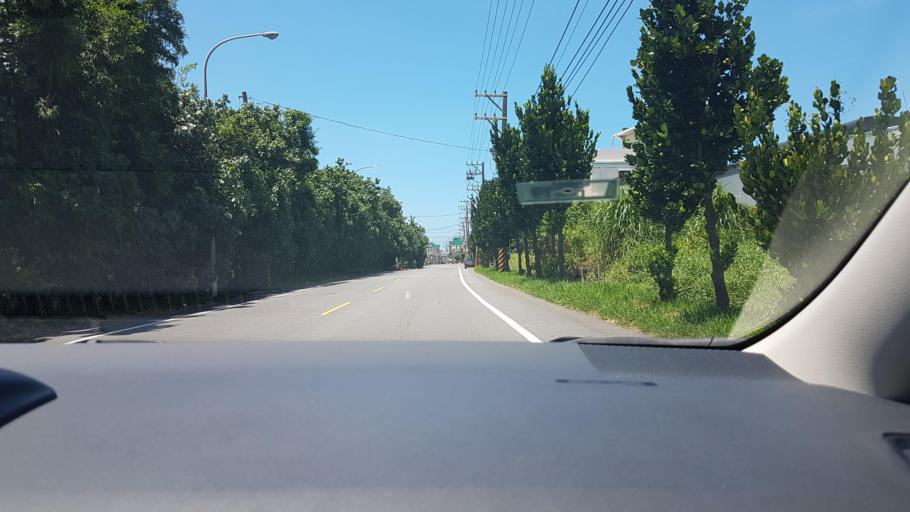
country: TW
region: Taiwan
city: Taoyuan City
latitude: 25.1069
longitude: 121.2571
